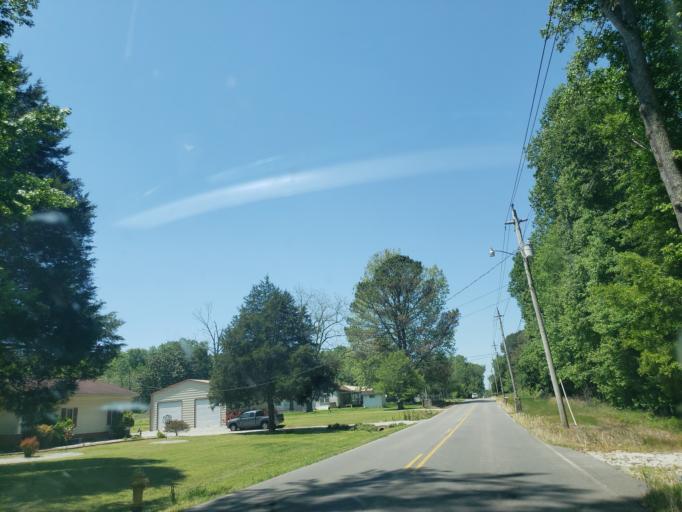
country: US
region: Alabama
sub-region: Madison County
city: Hazel Green
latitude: 34.9623
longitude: -86.6673
